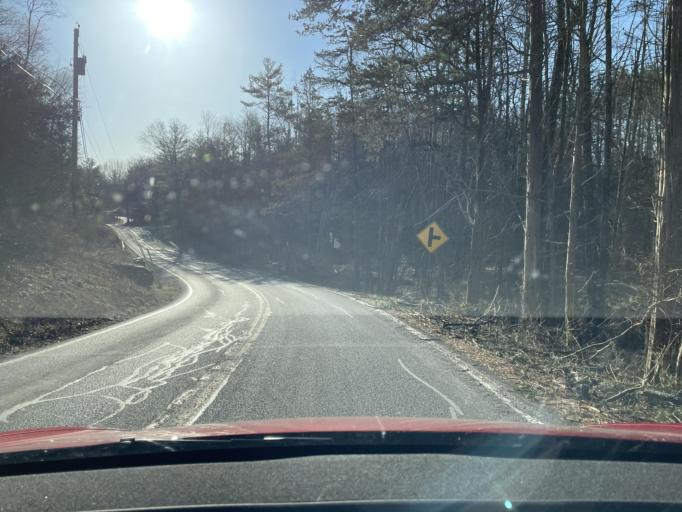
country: US
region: New York
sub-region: Ulster County
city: Zena
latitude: 42.0469
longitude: -74.0515
